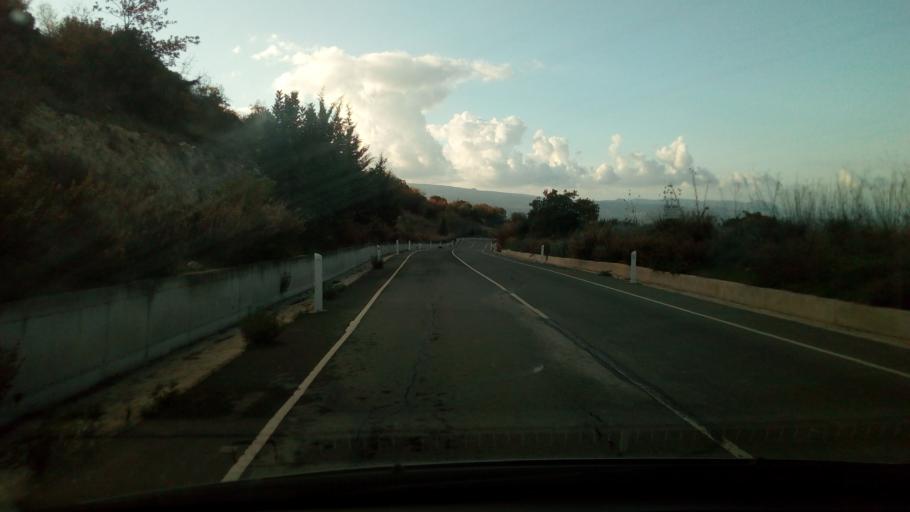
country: CY
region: Pafos
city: Tala
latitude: 34.9385
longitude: 32.5123
